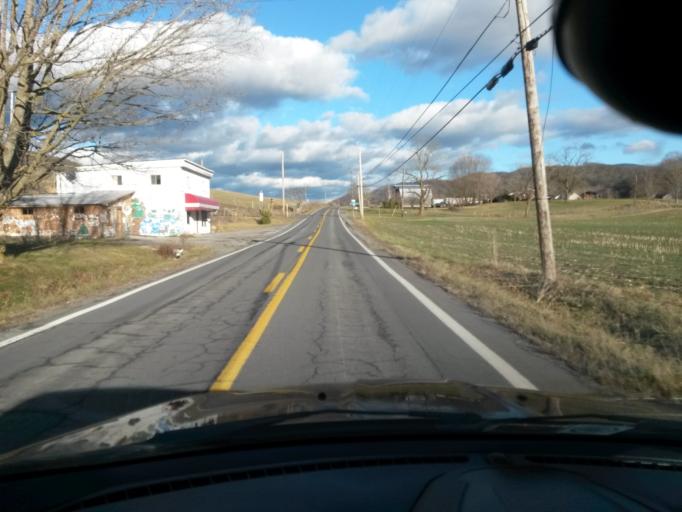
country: US
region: Virginia
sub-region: Giles County
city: Pearisburg
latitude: 37.4313
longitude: -80.7119
